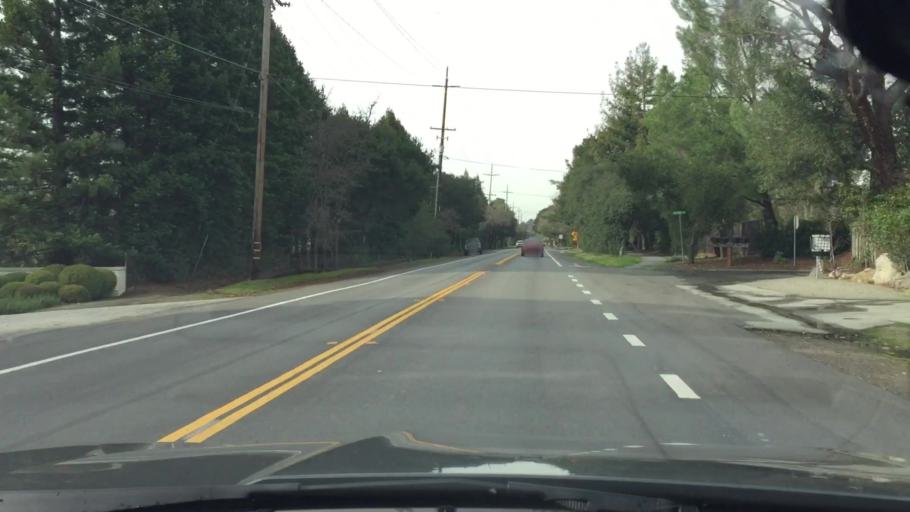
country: US
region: California
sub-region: San Mateo County
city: Woodside
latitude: 37.4341
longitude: -122.2581
